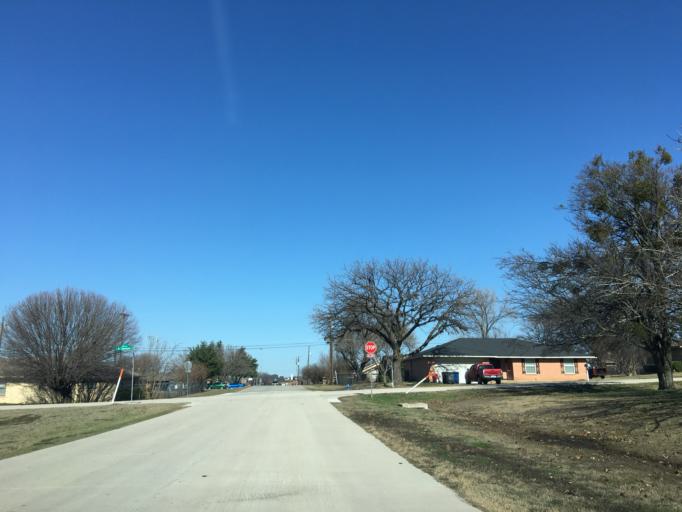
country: US
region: Texas
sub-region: Collin County
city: Prosper
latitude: 33.2388
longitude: -96.7983
